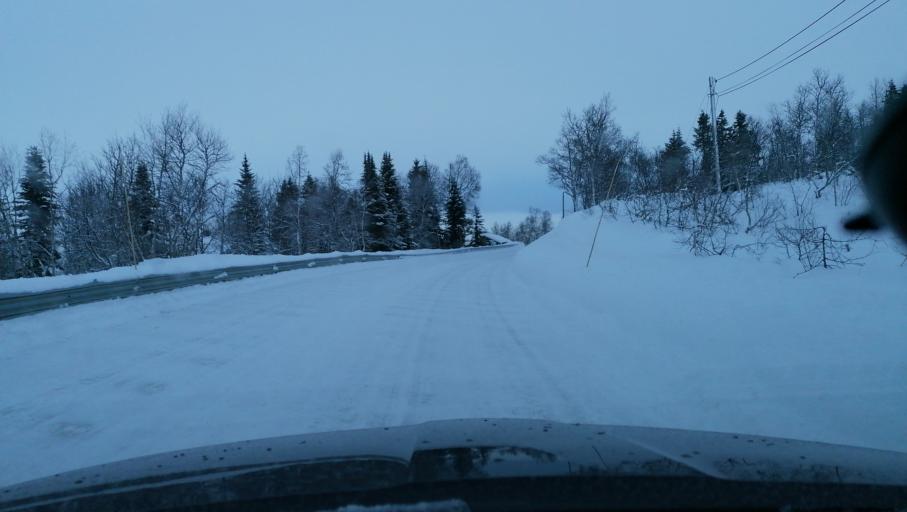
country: NO
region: Aust-Agder
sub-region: Bykle
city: Hovden
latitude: 59.6392
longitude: 7.4536
